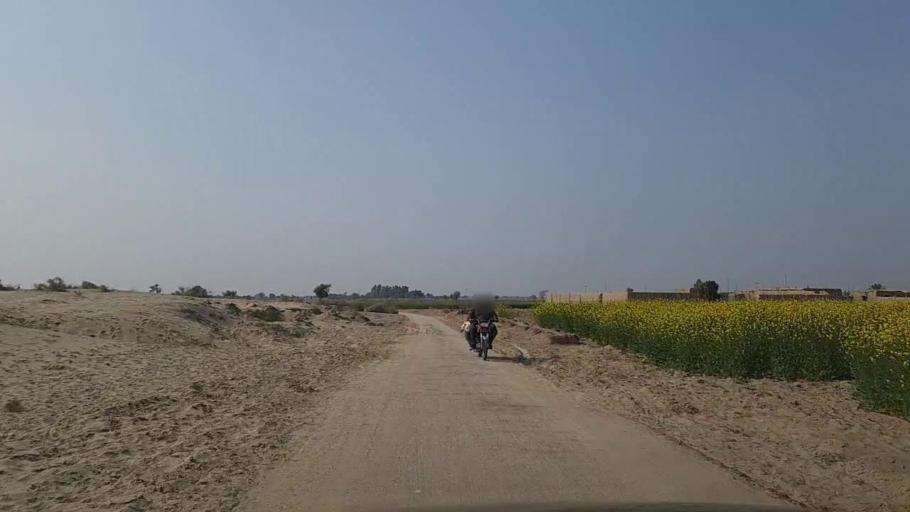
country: PK
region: Sindh
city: Daur
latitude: 26.3862
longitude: 68.4156
